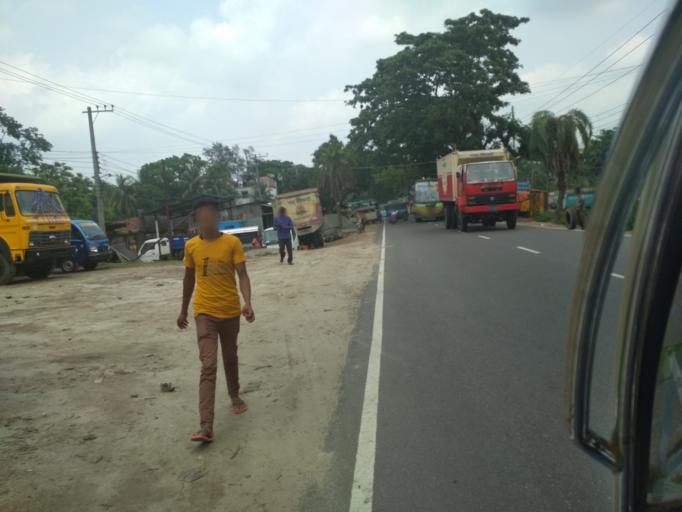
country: BD
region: Chittagong
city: Lakshmipur
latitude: 22.9421
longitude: 90.8436
